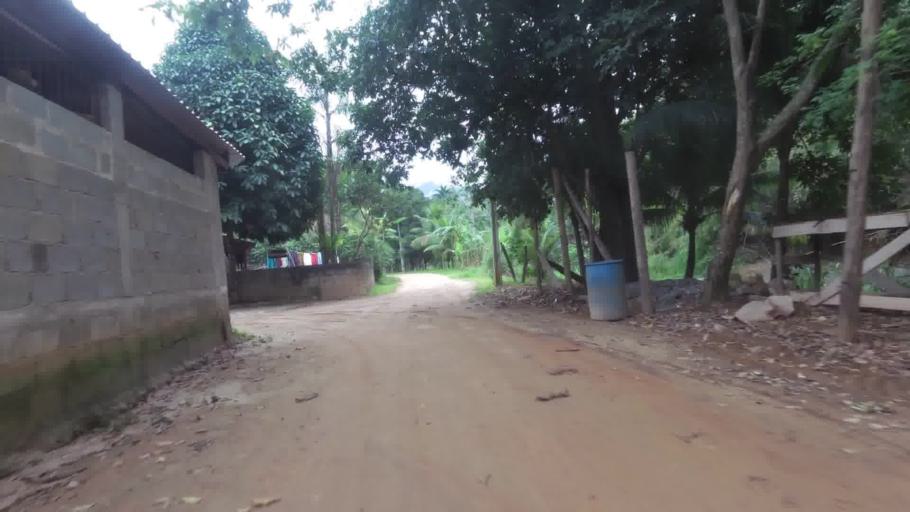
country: BR
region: Espirito Santo
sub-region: Iconha
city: Iconha
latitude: -20.7646
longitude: -40.8335
